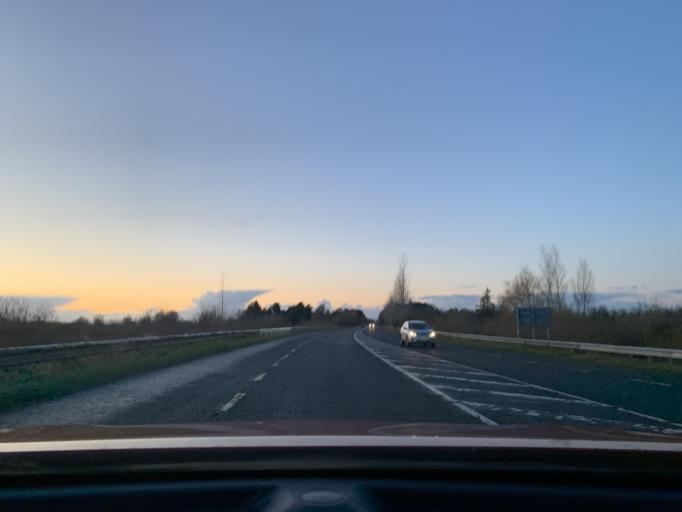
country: IE
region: Connaught
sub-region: County Leitrim
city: Carrick-on-Shannon
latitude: 53.9338
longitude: -8.0452
